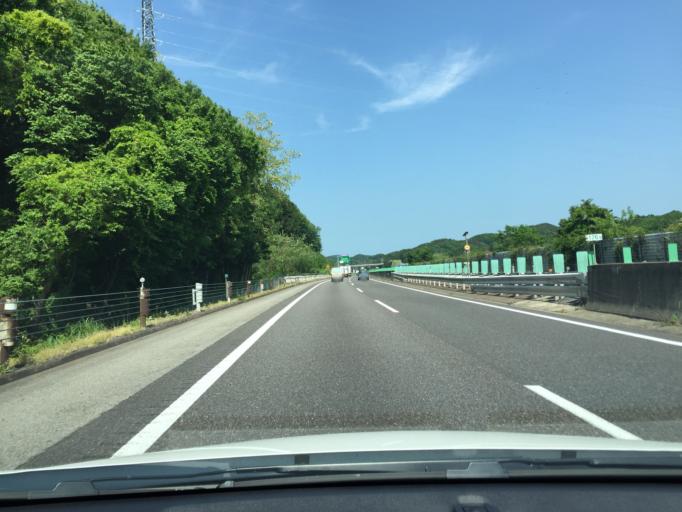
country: JP
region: Fukushima
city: Sukagawa
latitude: 37.1443
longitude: 140.2268
